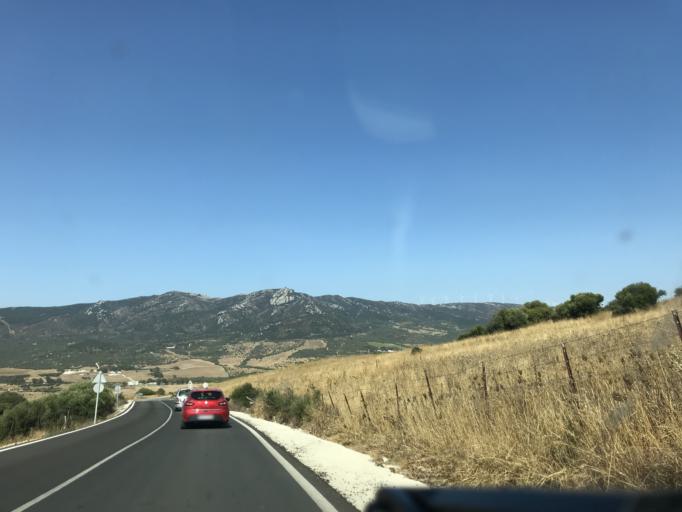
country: ES
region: Andalusia
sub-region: Provincia de Cadiz
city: Zahara de los Atunes
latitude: 36.1020
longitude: -5.7290
